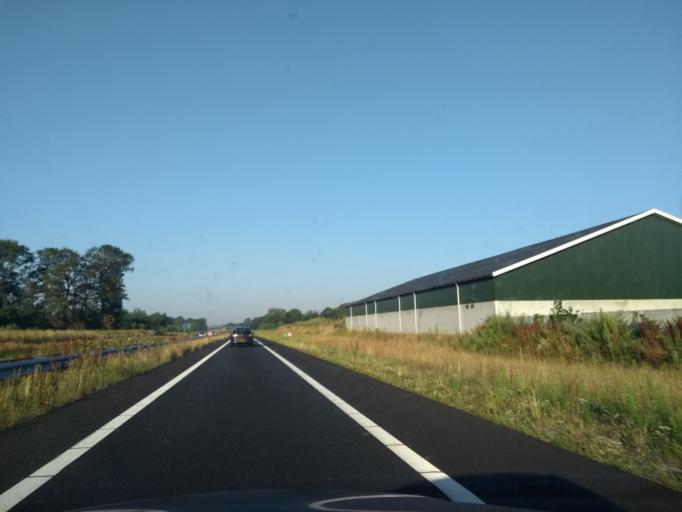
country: NL
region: Gelderland
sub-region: Berkelland
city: Eibergen
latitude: 52.1235
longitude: 6.6460
